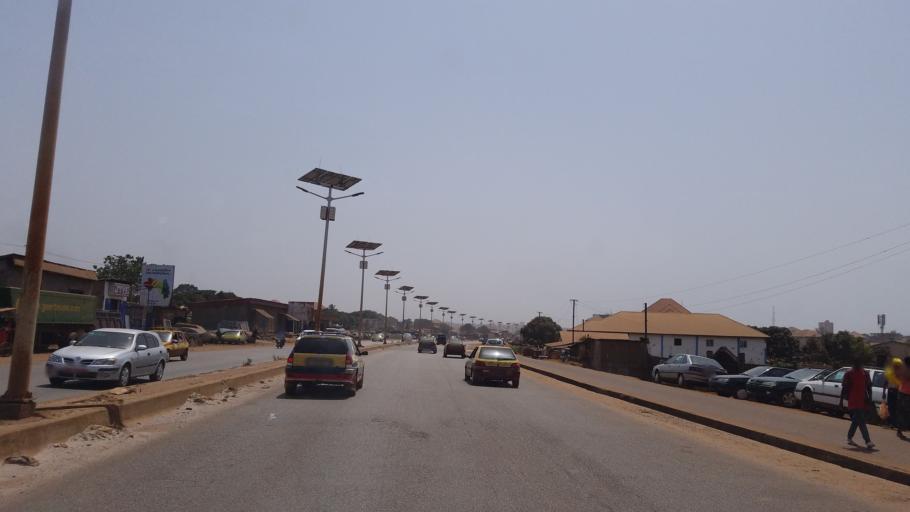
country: GN
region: Kindia
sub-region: Prefecture de Dubreka
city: Dubreka
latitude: 9.6595
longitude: -13.5664
